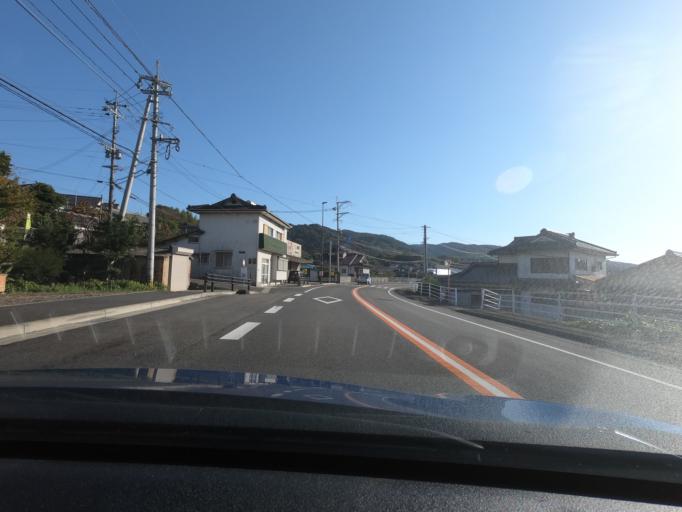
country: JP
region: Kumamoto
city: Minamata
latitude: 32.1774
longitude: 130.3838
